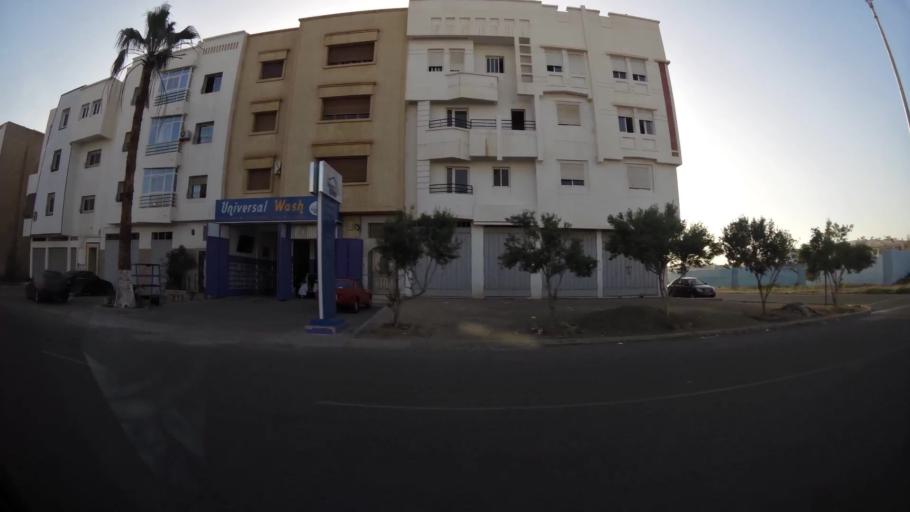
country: MA
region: Oued ed Dahab-Lagouira
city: Dakhla
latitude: 30.3946
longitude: -9.5425
